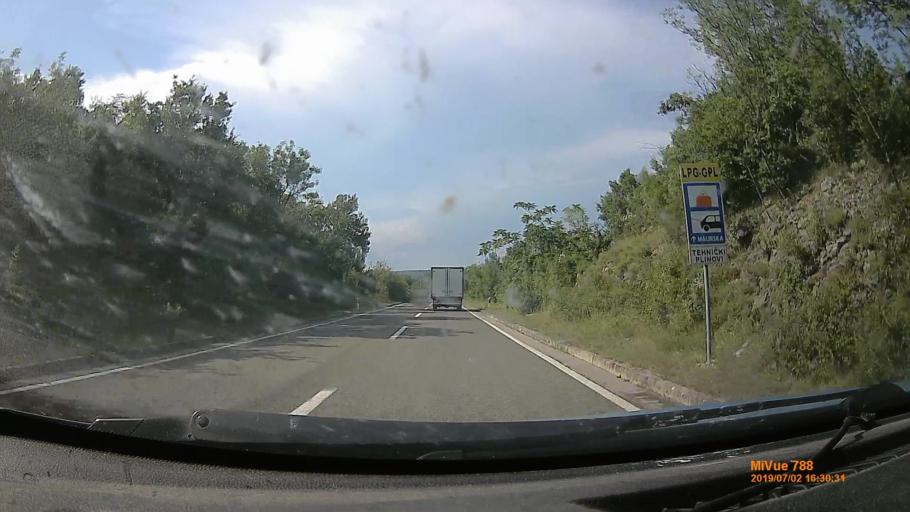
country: HR
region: Primorsko-Goranska
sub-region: Grad Krk
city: Krk
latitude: 45.0440
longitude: 14.4907
